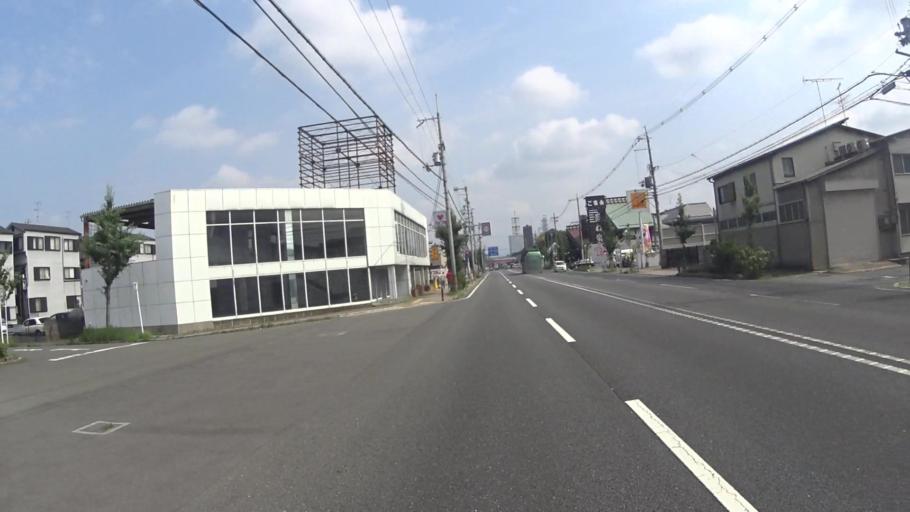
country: JP
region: Kyoto
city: Muko
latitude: 34.9485
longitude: 135.7453
